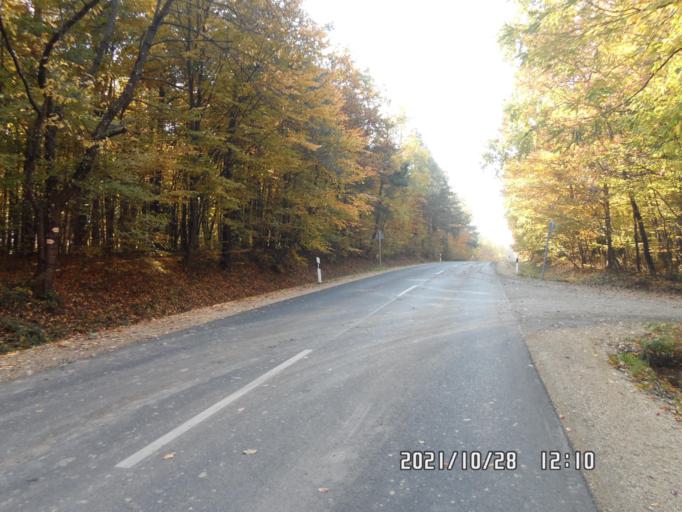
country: SI
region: Hodos-Hodos
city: Hodos
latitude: 46.7796
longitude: 16.3609
